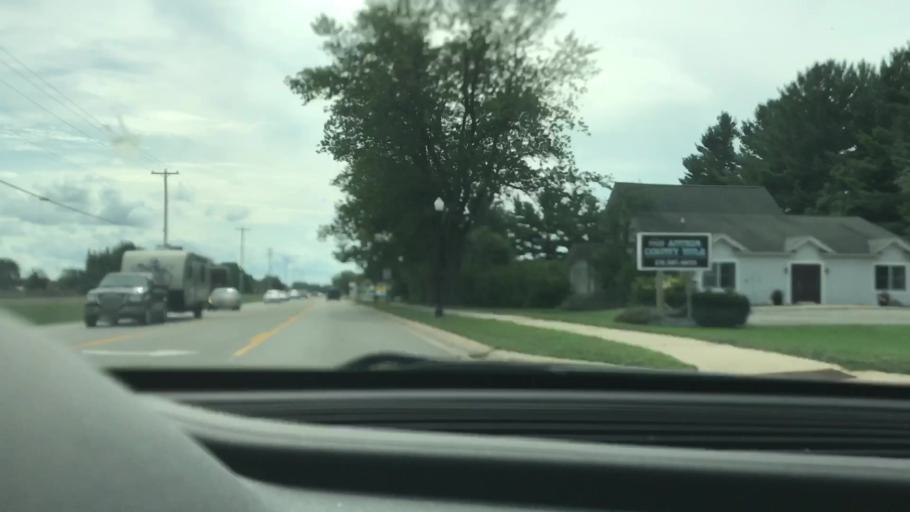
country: US
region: Michigan
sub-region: Antrim County
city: Mancelona
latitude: 44.8988
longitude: -85.0645
